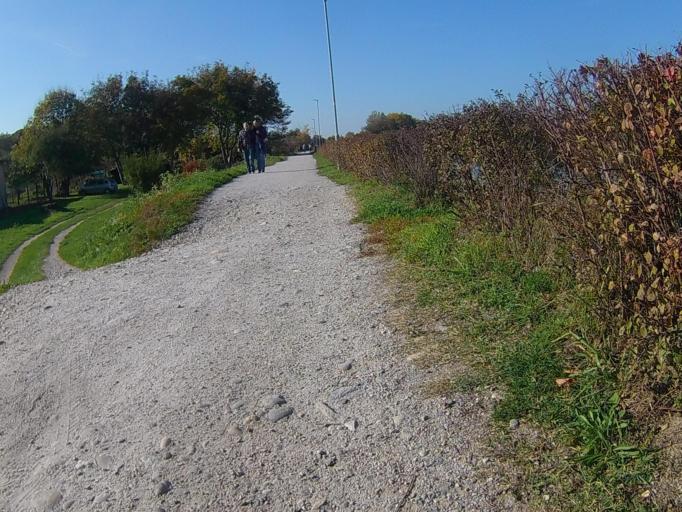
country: SI
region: Ptuj
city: Ptuj
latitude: 46.4183
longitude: 15.8642
